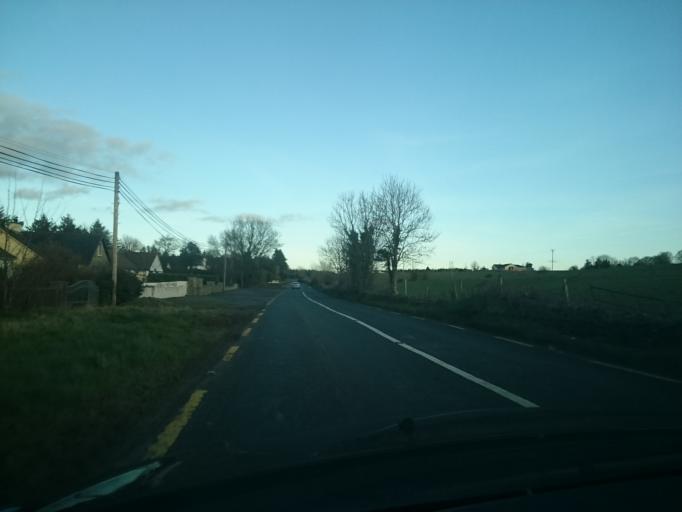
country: IE
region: Connaught
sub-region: Maigh Eo
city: Kiltamagh
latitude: 53.7973
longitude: -9.1019
